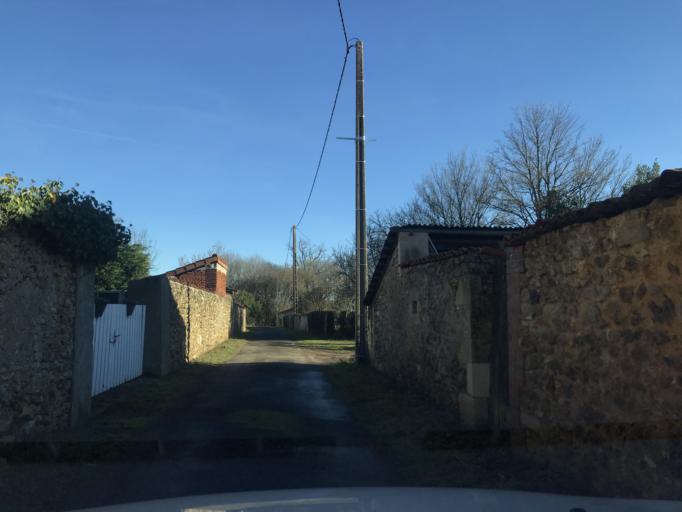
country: FR
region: Poitou-Charentes
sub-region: Departement de la Charente
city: Saint-Claud
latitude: 45.8504
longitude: 0.5071
